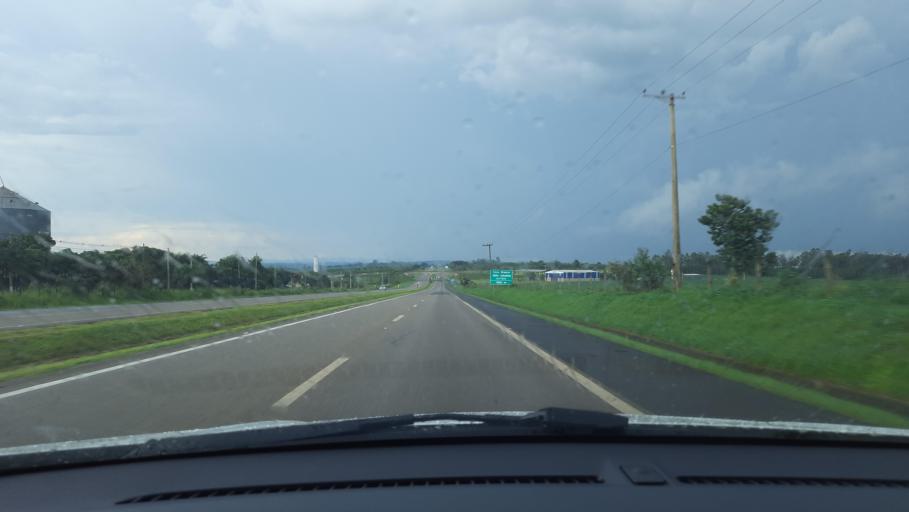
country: BR
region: Sao Paulo
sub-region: Casa Branca
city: Casa Branca
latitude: -21.7542
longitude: -47.0711
